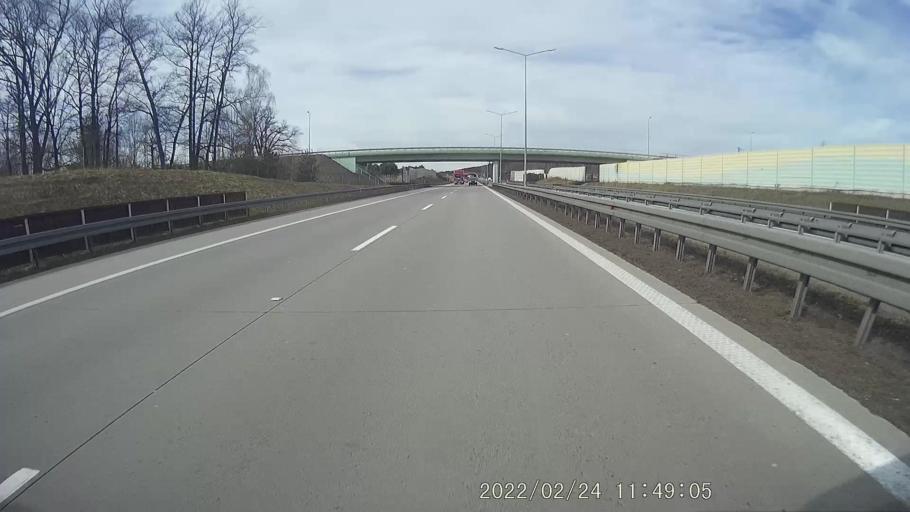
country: PL
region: Lower Silesian Voivodeship
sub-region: Powiat polkowicki
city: Radwanice
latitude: 51.5905
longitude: 15.9587
